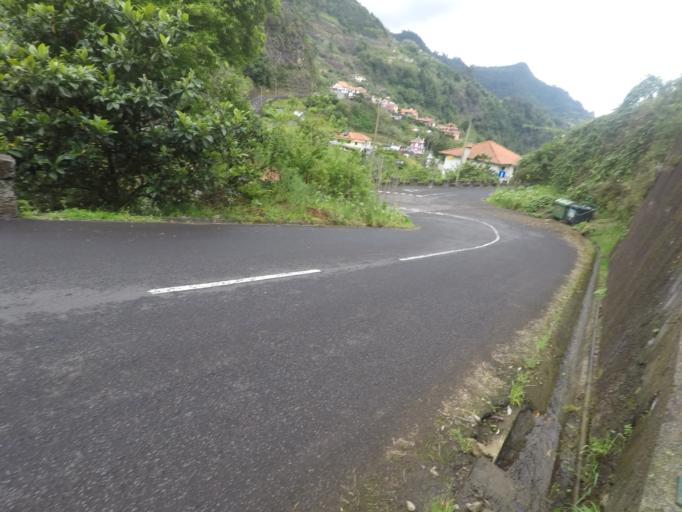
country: PT
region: Madeira
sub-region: Santana
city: Santana
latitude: 32.7633
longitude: -16.8757
